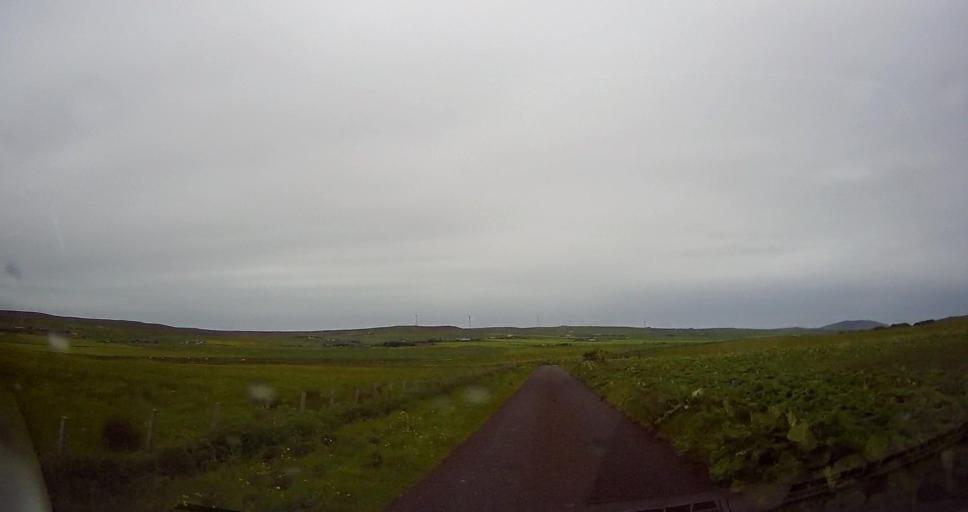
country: GB
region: Scotland
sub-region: Orkney Islands
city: Orkney
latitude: 59.1170
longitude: -3.0807
